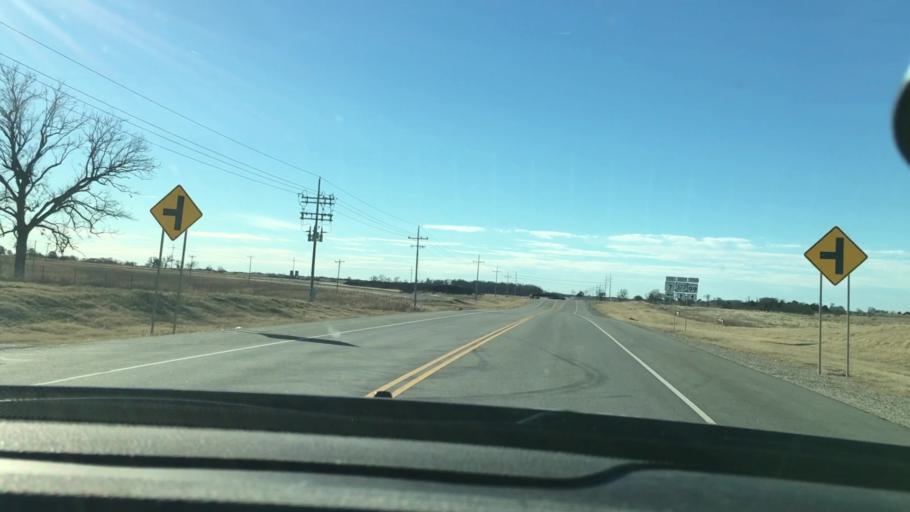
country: US
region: Oklahoma
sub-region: Johnston County
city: Tishomingo
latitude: 34.3665
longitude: -96.6369
